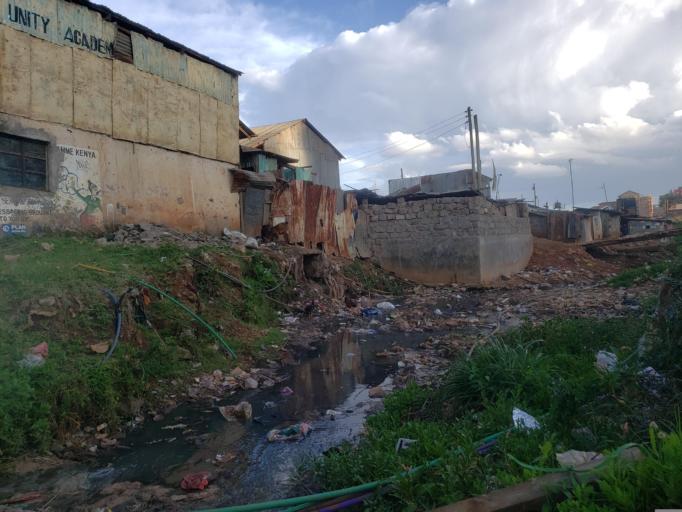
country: KE
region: Nairobi Area
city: Nairobi
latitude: -1.3107
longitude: 36.7720
